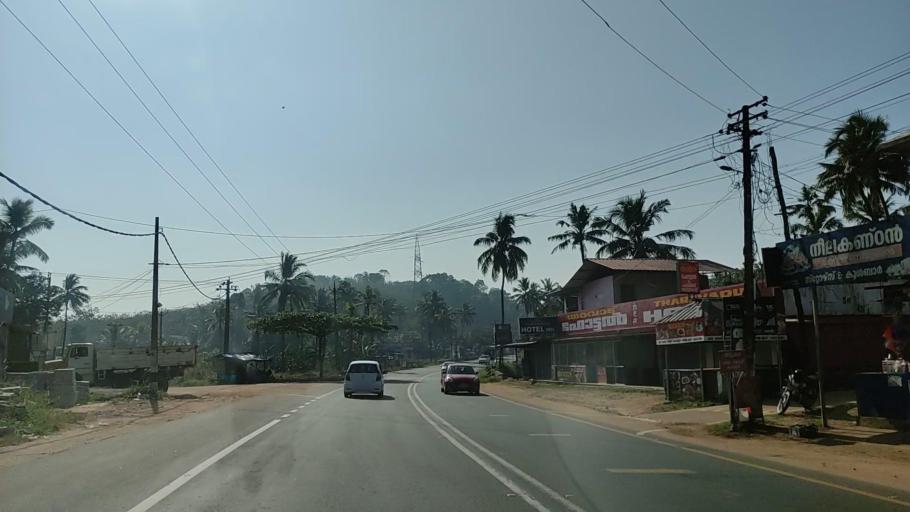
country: IN
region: Kerala
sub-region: Kollam
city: Punalur
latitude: 8.9057
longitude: 76.8551
